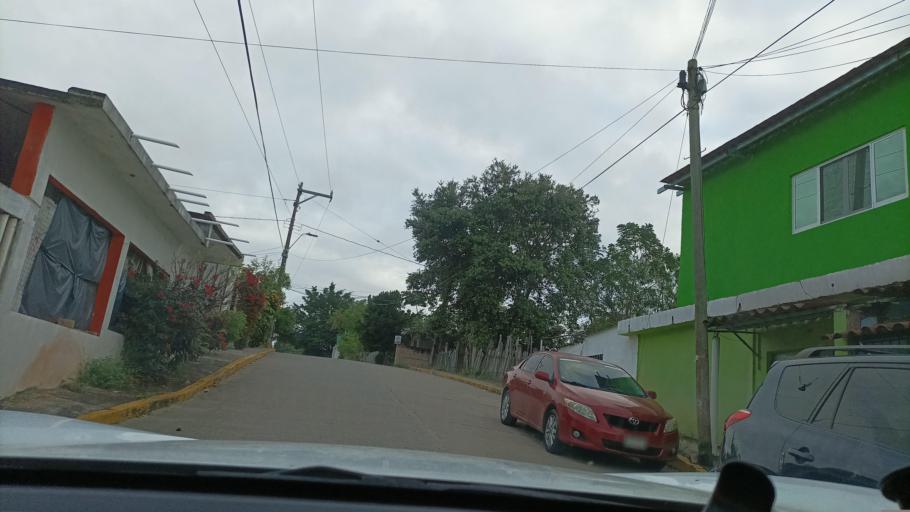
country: MX
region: Veracruz
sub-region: Cosoleacaque
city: Hermenegildo J. Aldana
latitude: 17.9938
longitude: -94.6102
